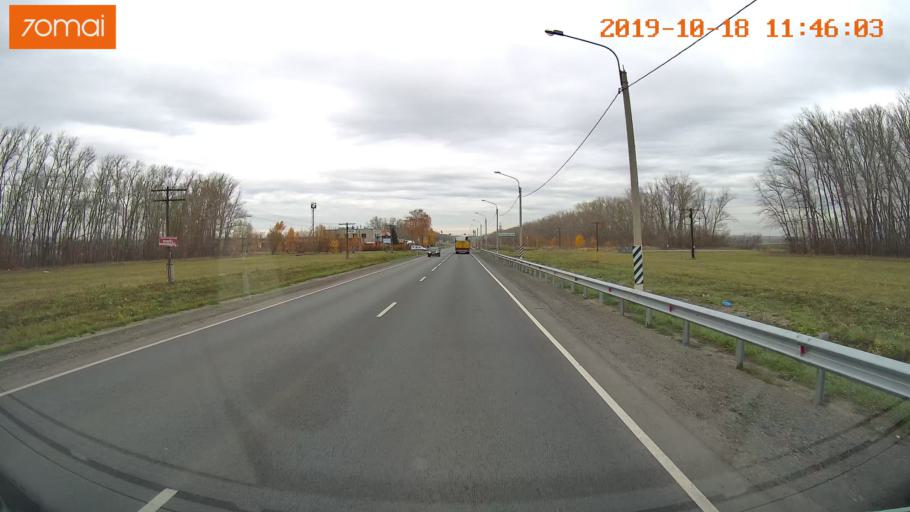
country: RU
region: Rjazan
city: Mikhaylov
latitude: 54.2161
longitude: 38.9784
